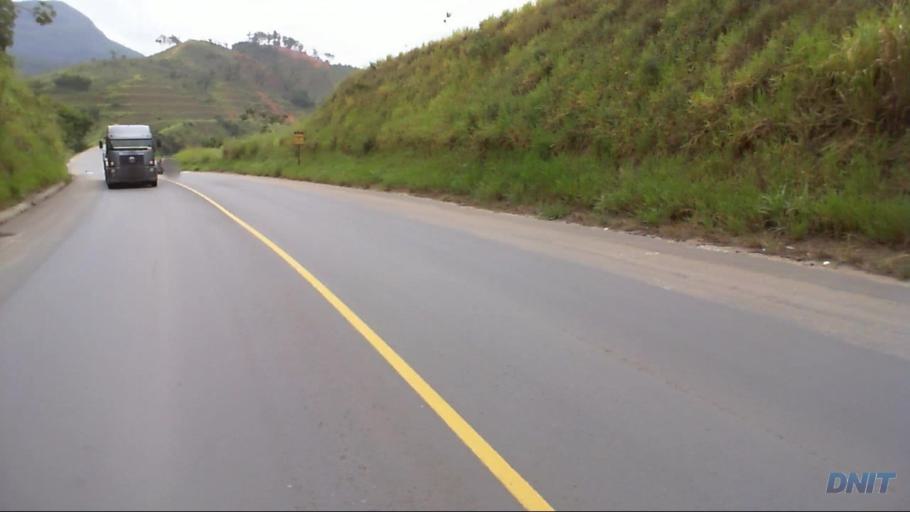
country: BR
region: Minas Gerais
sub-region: Coronel Fabriciano
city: Coronel Fabriciano
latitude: -19.5345
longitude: -42.6728
